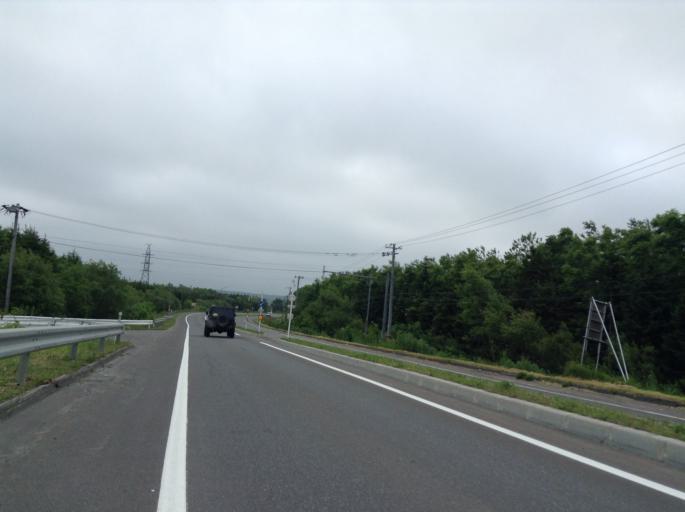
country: JP
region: Hokkaido
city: Wakkanai
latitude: 45.3702
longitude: 141.7241
